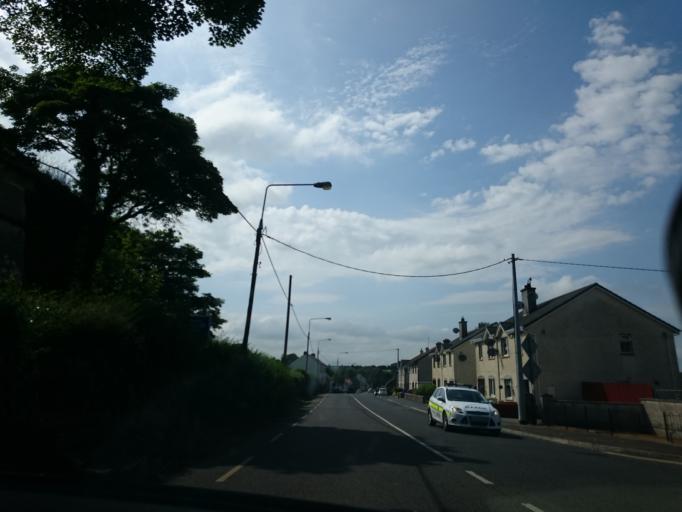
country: IE
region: Leinster
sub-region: Kilkenny
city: Thomastown
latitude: 52.5349
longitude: -7.2241
